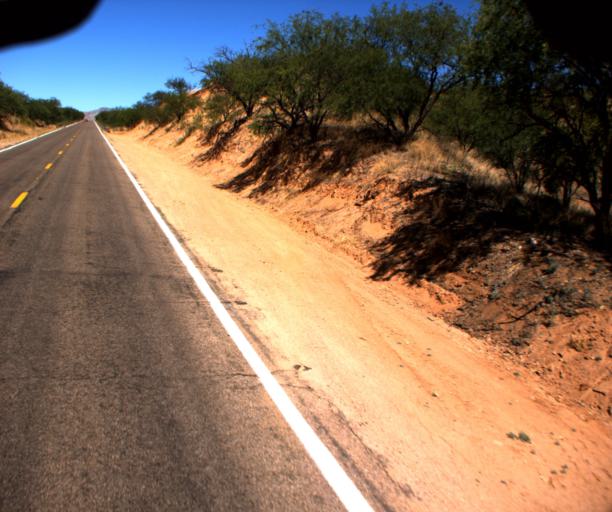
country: US
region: Arizona
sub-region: Santa Cruz County
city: Rio Rico
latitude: 31.4297
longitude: -110.9817
